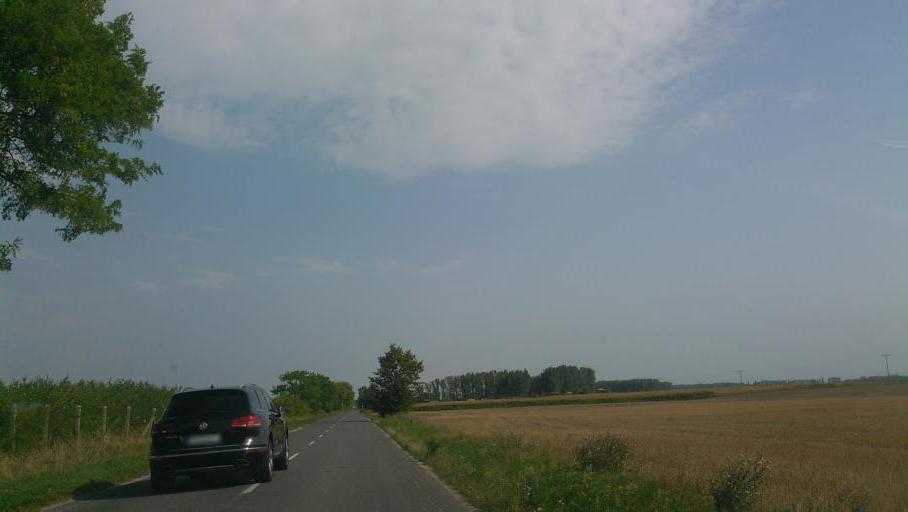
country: SK
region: Trnavsky
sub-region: Okres Dunajska Streda
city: Velky Meder
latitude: 47.9279
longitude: 17.7320
